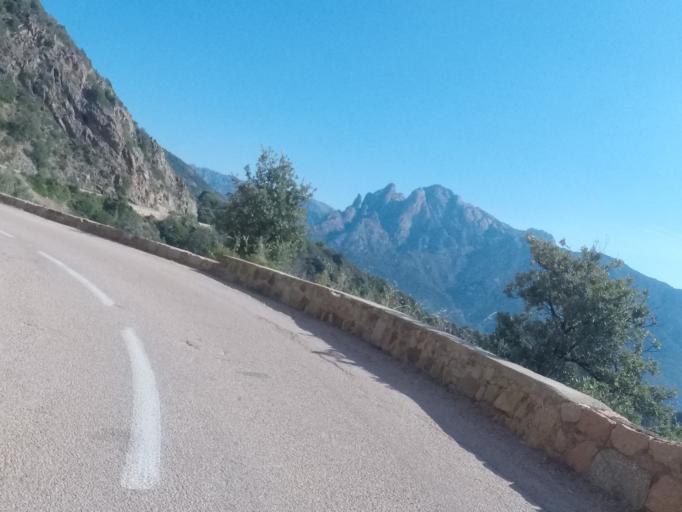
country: FR
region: Corsica
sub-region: Departement de la Corse-du-Sud
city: Cargese
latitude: 42.2910
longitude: 8.6791
